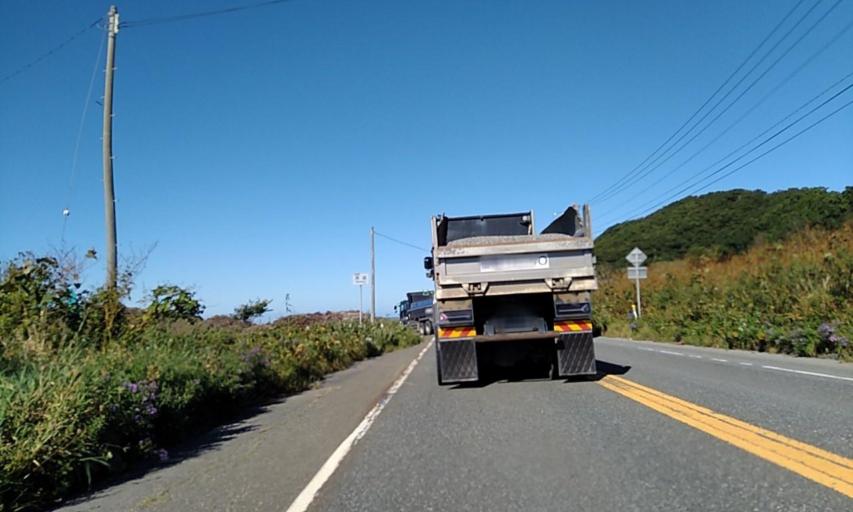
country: JP
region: Hokkaido
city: Shizunai-furukawacho
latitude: 42.4503
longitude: 142.1922
